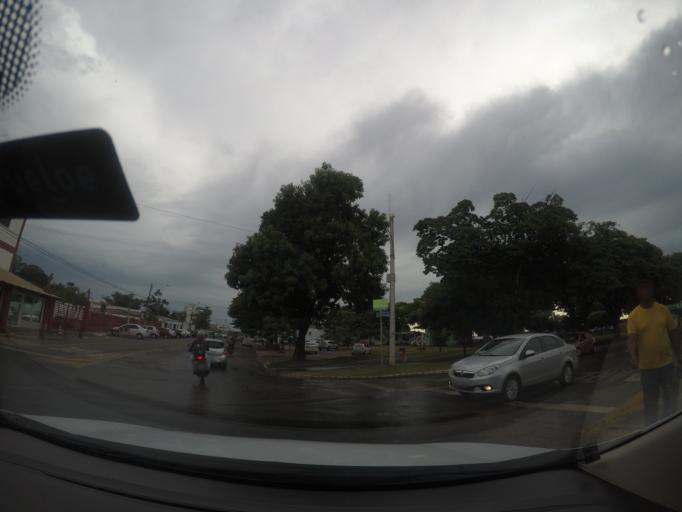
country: BR
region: Goias
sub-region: Goiania
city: Goiania
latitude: -16.6667
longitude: -49.3004
